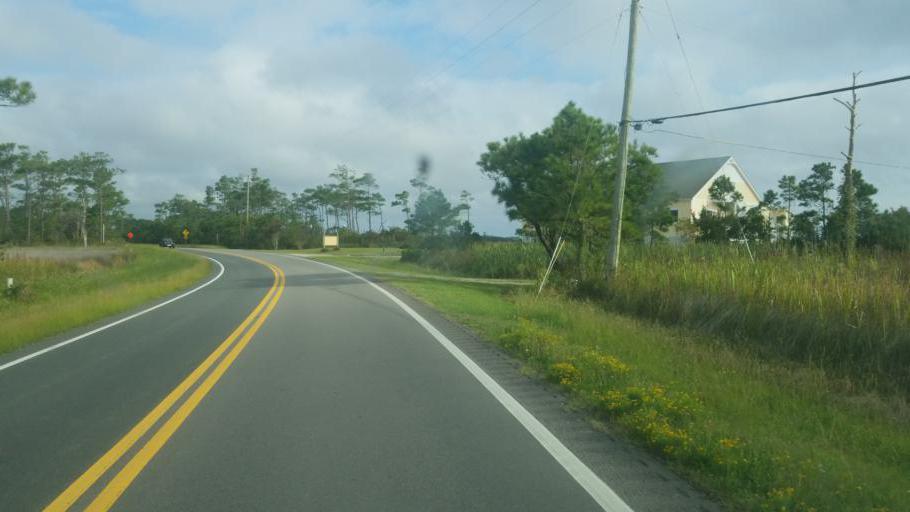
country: US
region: North Carolina
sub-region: Dare County
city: Wanchese
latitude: 35.8682
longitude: -75.6498
